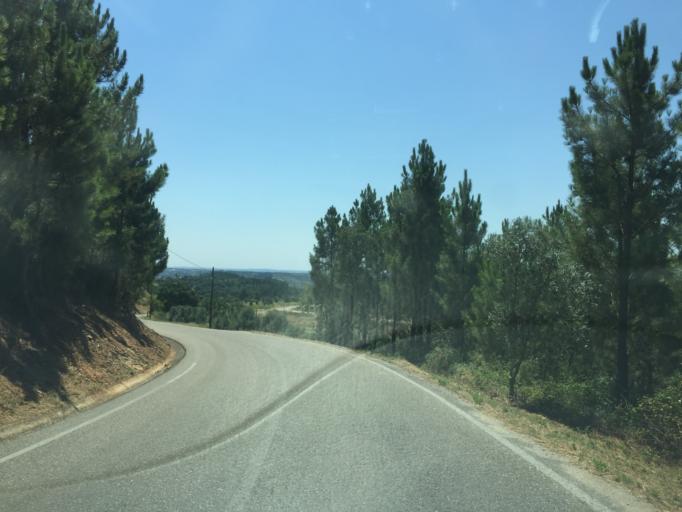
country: PT
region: Santarem
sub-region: Ferreira do Zezere
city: Ferreira do Zezere
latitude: 39.5970
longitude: -8.3009
